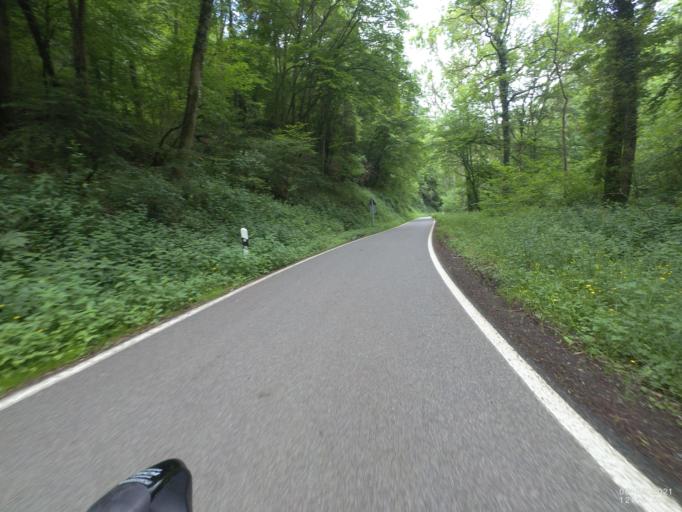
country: DE
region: Rheinland-Pfalz
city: Hatzenport
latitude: 50.2336
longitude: 7.4019
